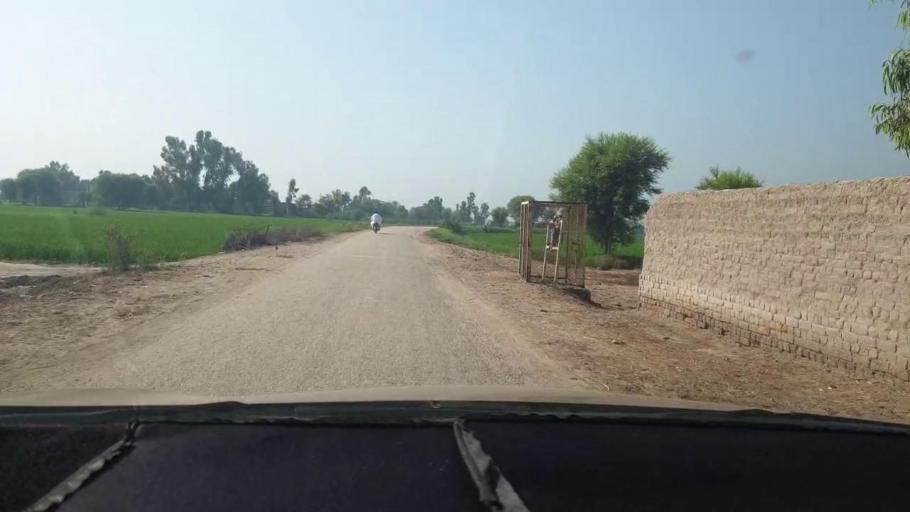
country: PK
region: Sindh
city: Kambar
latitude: 27.6003
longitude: 68.0935
